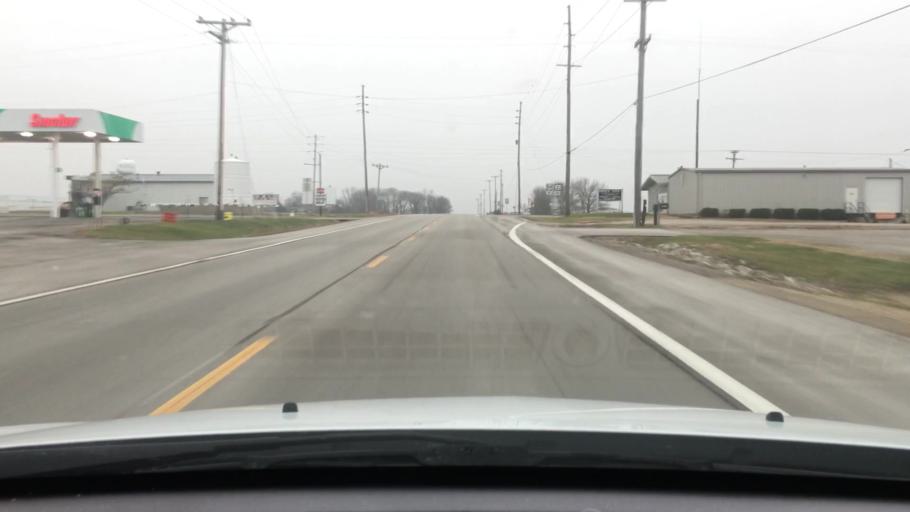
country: US
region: Missouri
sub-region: Audrain County
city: Mexico
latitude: 39.1635
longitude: -91.8309
